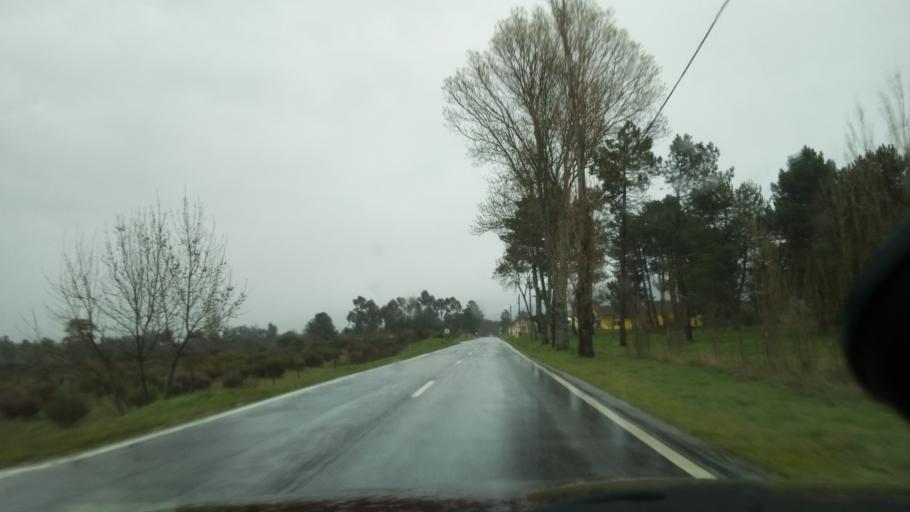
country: PT
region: Guarda
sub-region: Fornos de Algodres
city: Fornos de Algodres
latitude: 40.5355
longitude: -7.5574
